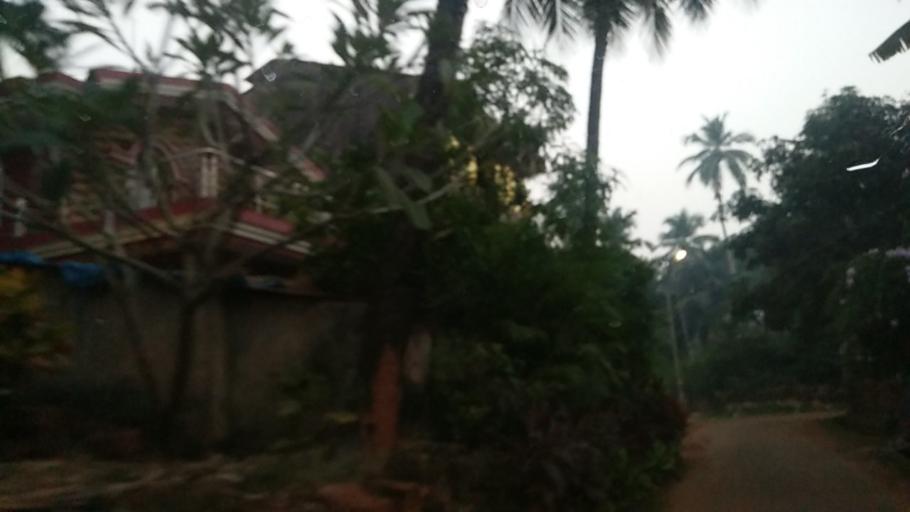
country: IN
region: Goa
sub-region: South Goa
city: Madgaon
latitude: 15.2847
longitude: 73.9550
